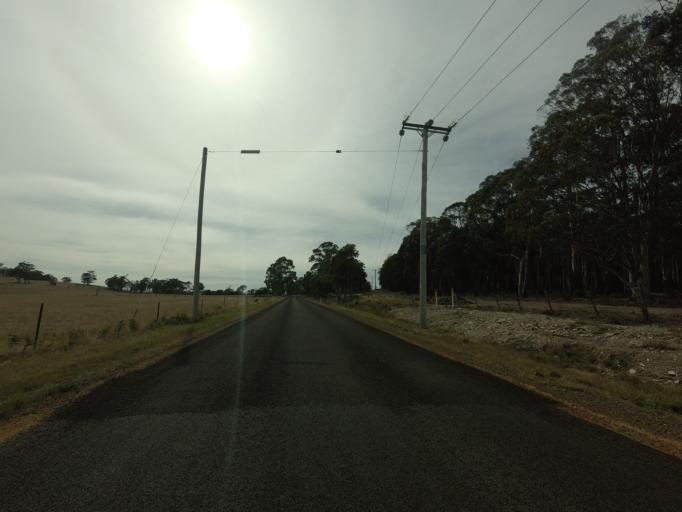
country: AU
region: Tasmania
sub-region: Sorell
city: Sorell
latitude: -42.4261
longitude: 147.4844
